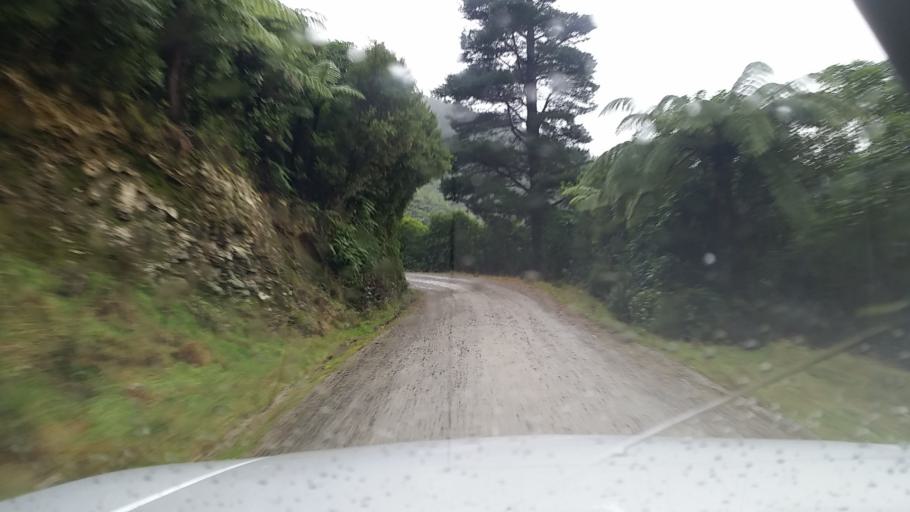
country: NZ
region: Marlborough
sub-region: Marlborough District
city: Picton
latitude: -41.1422
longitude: 174.0471
